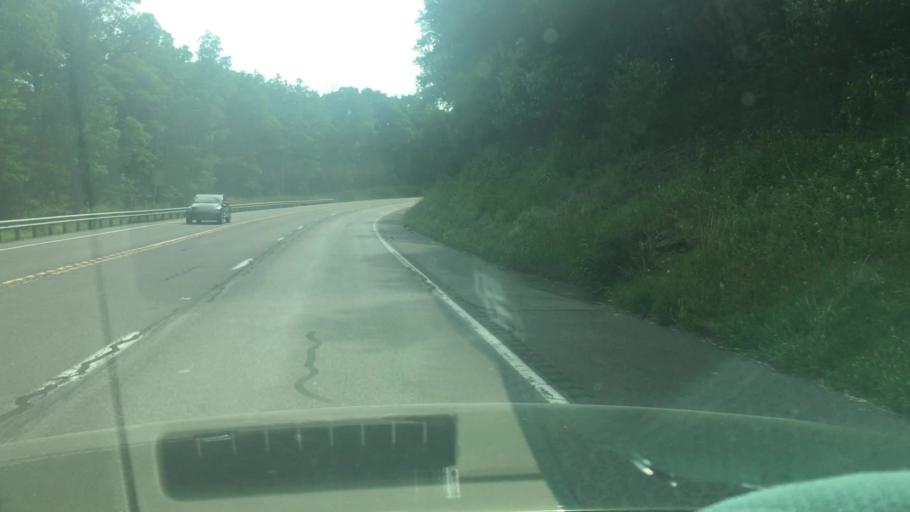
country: US
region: Pennsylvania
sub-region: Northumberland County
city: Elysburg
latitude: 40.8501
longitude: -76.5342
